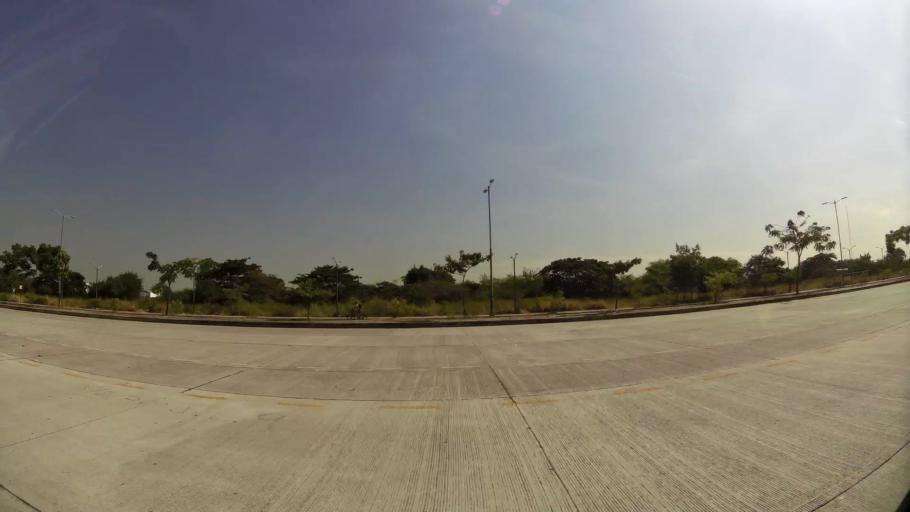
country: EC
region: Guayas
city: Eloy Alfaro
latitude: -2.1019
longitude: -79.9052
